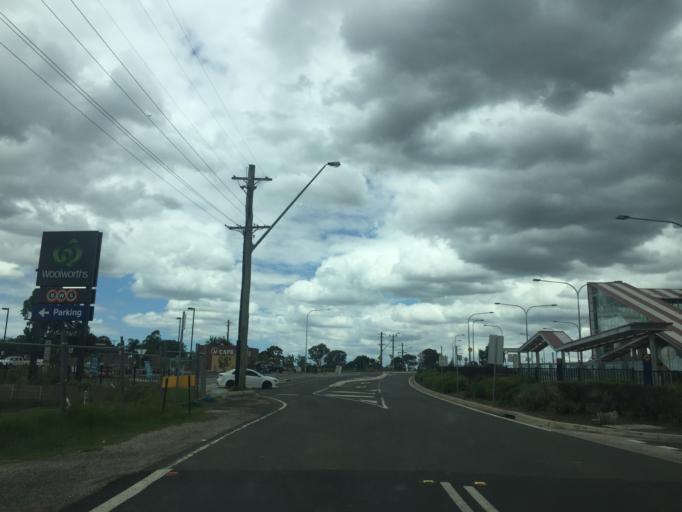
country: AU
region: New South Wales
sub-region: Blacktown
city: Riverstone
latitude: -33.7036
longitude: 150.8740
